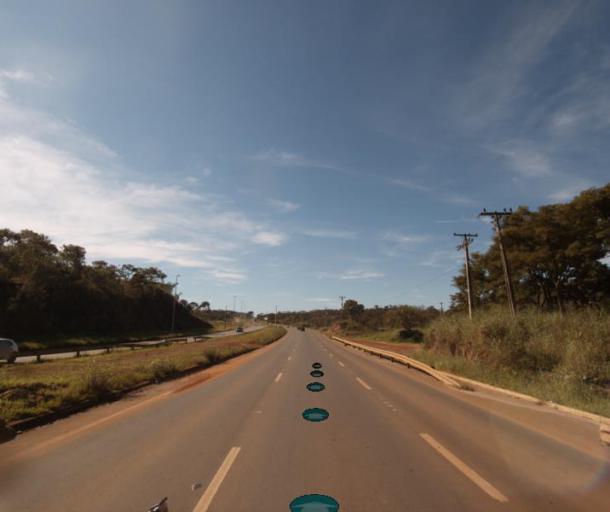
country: BR
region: Federal District
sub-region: Brasilia
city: Brasilia
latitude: -15.7844
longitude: -48.2321
